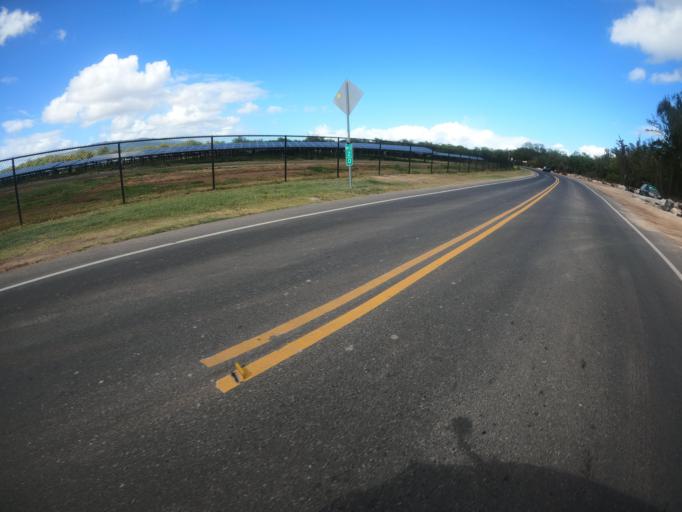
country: US
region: Hawaii
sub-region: Honolulu County
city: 'Ewa Villages
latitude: 21.3012
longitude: -158.0594
